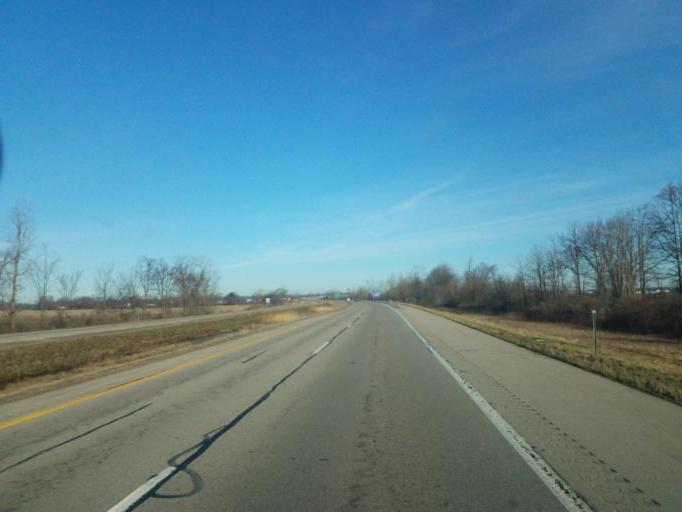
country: US
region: Michigan
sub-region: Gratiot County
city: Ithaca
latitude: 43.2764
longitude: -84.5711
